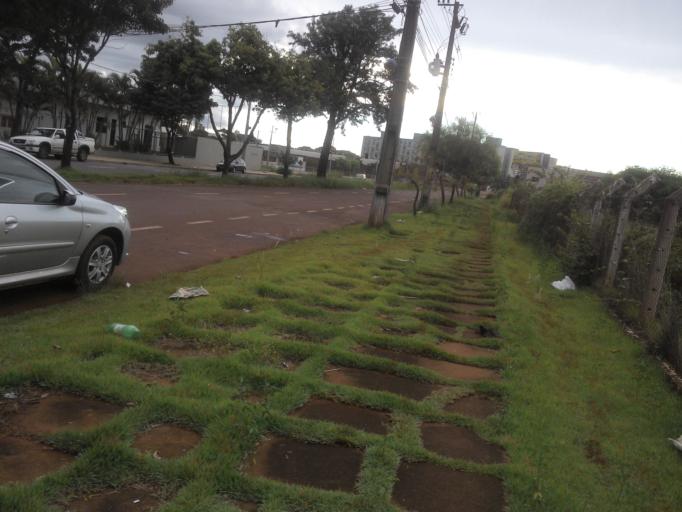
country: BR
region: Parana
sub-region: Maringa
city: Maringa
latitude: -23.4231
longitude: -51.9127
